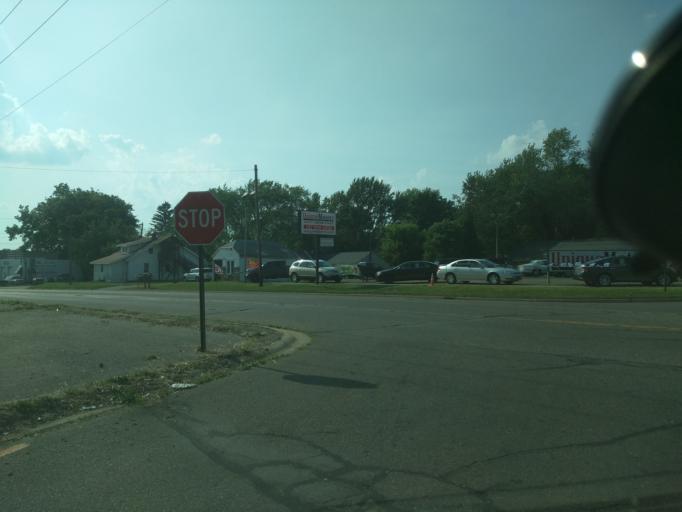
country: US
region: Michigan
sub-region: Jackson County
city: Jackson
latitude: 42.2546
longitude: -84.4382
